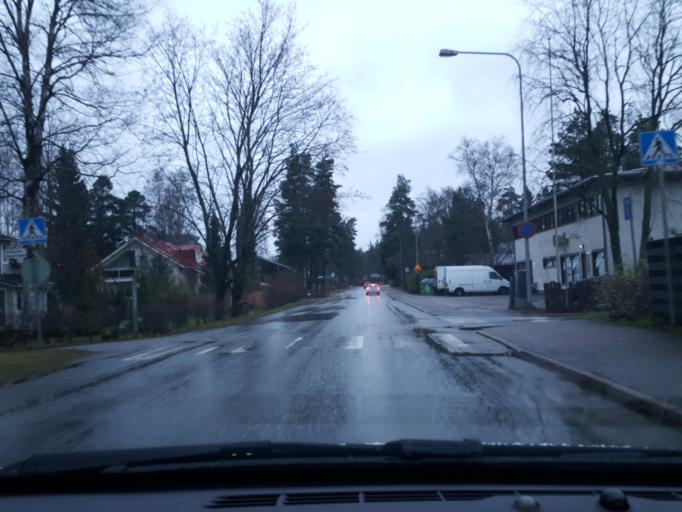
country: FI
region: Uusimaa
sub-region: Helsinki
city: Vantaa
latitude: 60.3040
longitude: 25.0380
